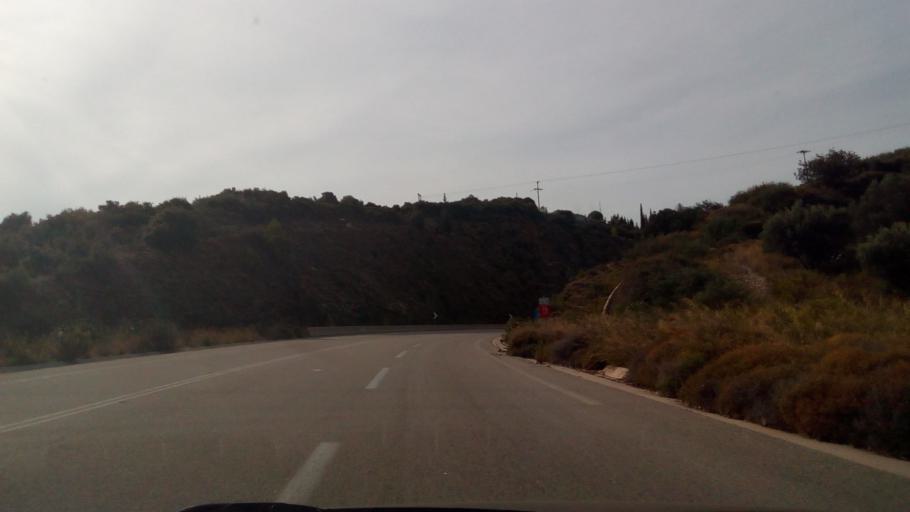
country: GR
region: West Greece
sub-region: Nomos Aitolias kai Akarnanias
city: Nafpaktos
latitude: 38.4028
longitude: 21.8362
